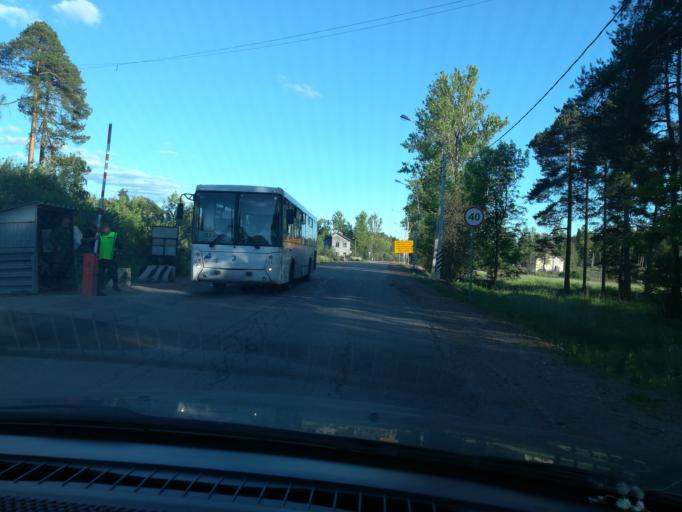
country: RU
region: Leningrad
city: Lesogorskiy
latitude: 61.0485
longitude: 28.9269
